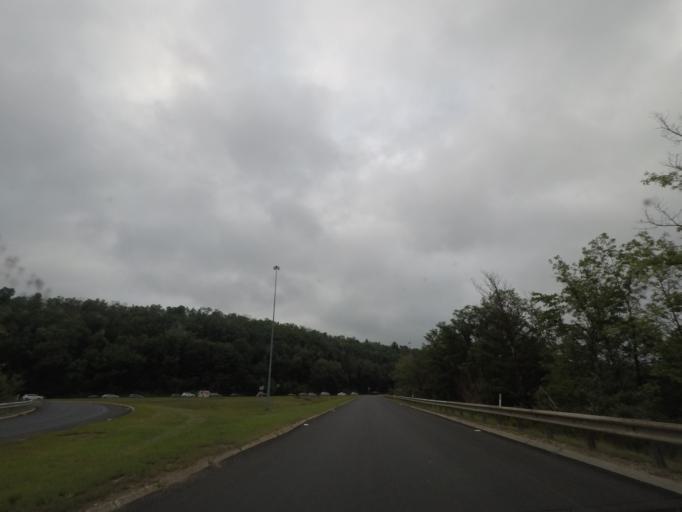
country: US
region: Massachusetts
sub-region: Worcester County
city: Sturbridge
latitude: 42.1177
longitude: -72.0715
